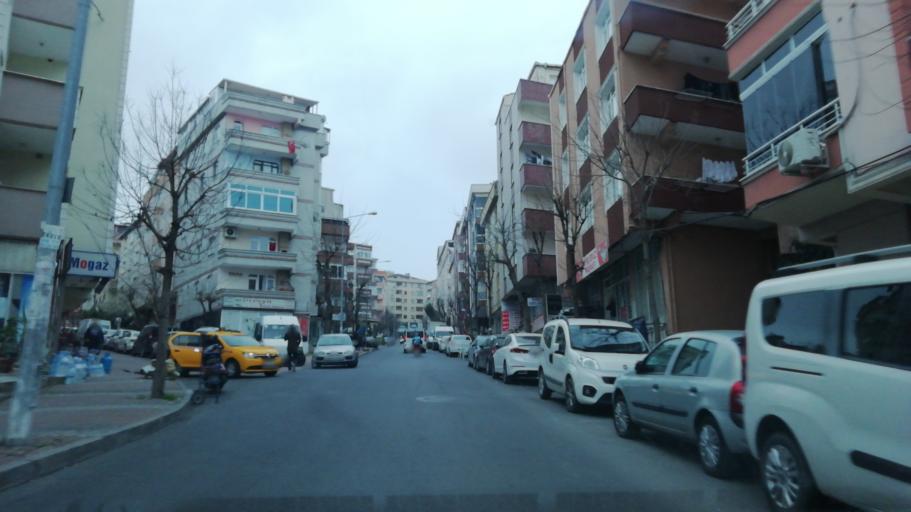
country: TR
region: Istanbul
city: Bahcelievler
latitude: 41.0058
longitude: 28.8498
